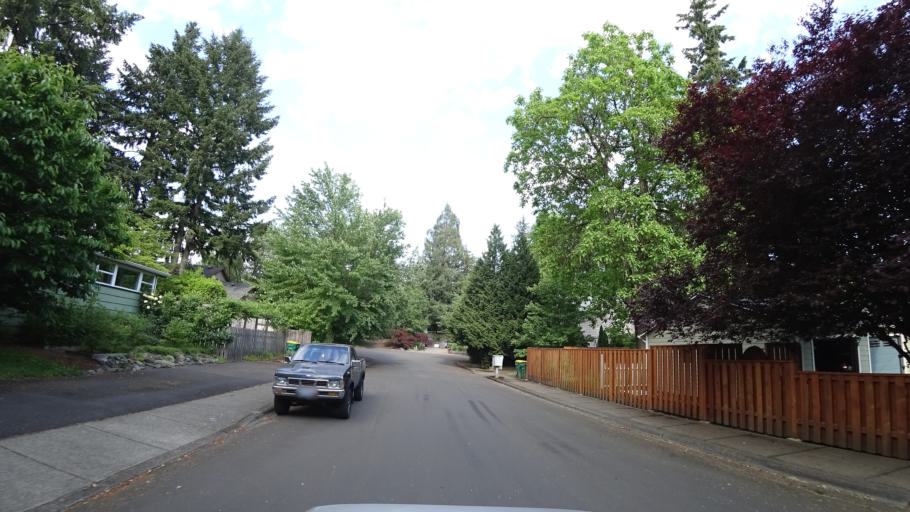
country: US
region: Oregon
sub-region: Washington County
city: Garden Home-Whitford
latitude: 45.4622
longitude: -122.7499
